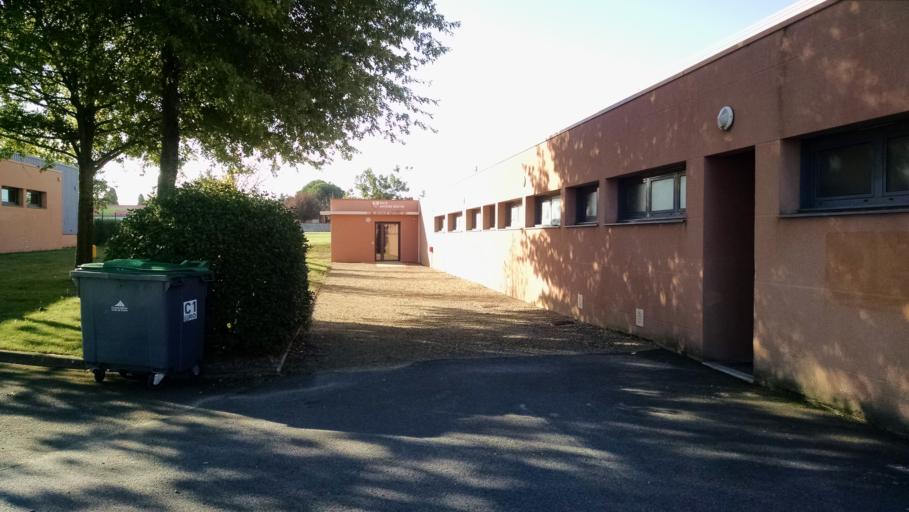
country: FR
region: Pays de la Loire
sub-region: Departement de la Loire-Atlantique
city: Remouille
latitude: 47.0537
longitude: -1.3823
